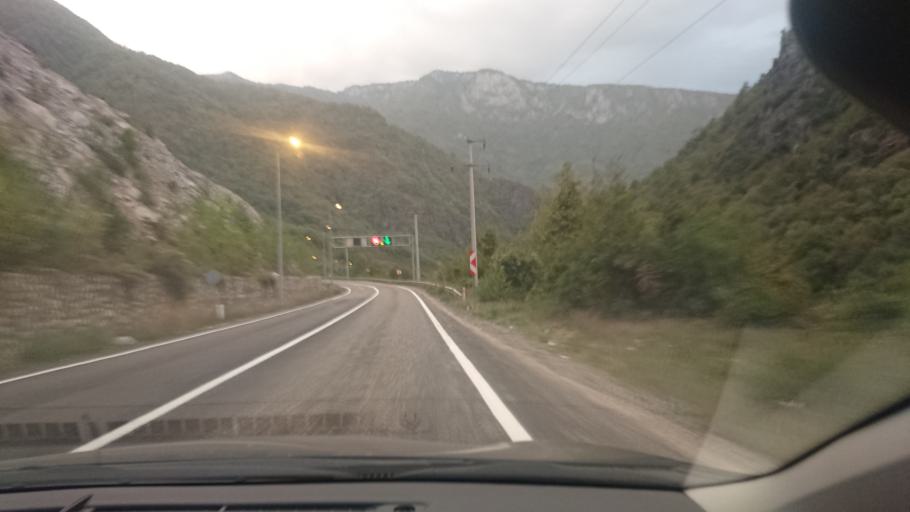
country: TR
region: Karabuk
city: Yenice
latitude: 41.1585
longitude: 32.4730
